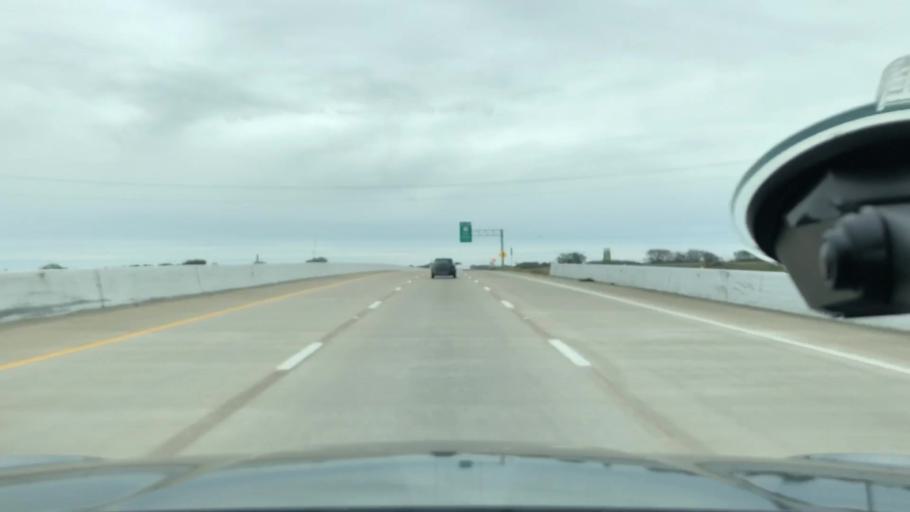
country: US
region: Texas
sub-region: Ellis County
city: Italy
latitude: 32.1765
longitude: -96.9094
